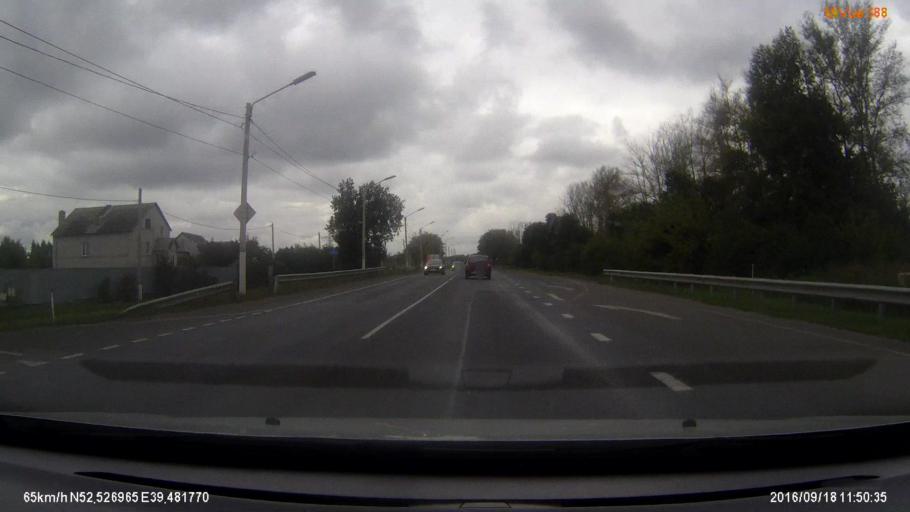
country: RU
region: Lipetsk
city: Syrskoye
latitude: 52.5272
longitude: 39.4822
